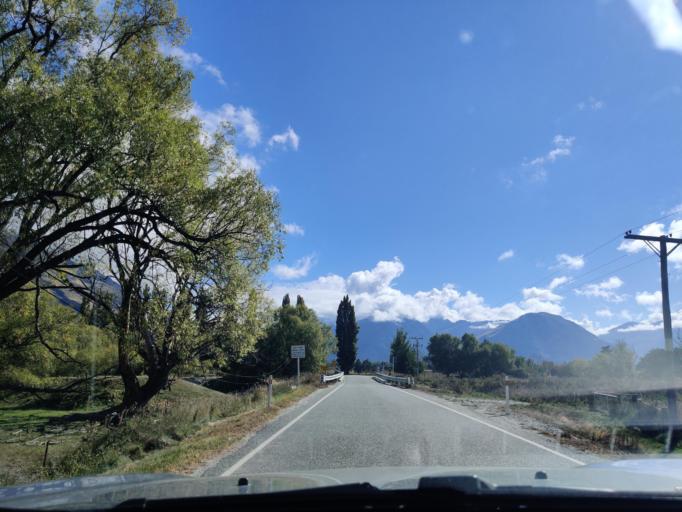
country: NZ
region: Otago
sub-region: Queenstown-Lakes District
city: Queenstown
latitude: -44.8010
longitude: 168.3986
